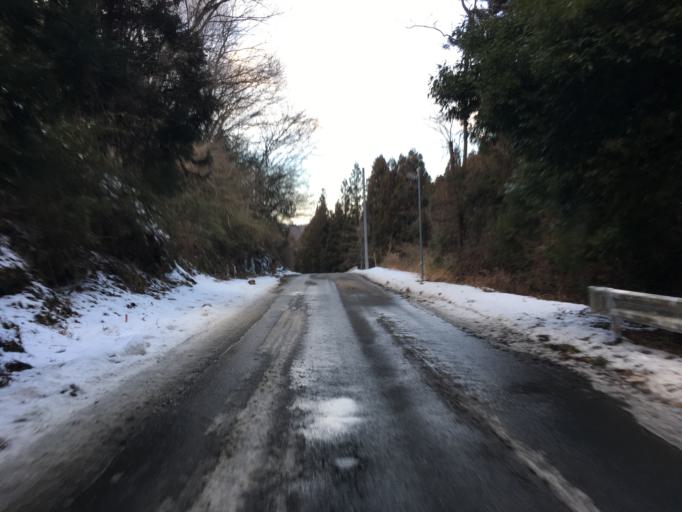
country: JP
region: Fukushima
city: Fukushima-shi
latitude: 37.6469
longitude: 140.5896
